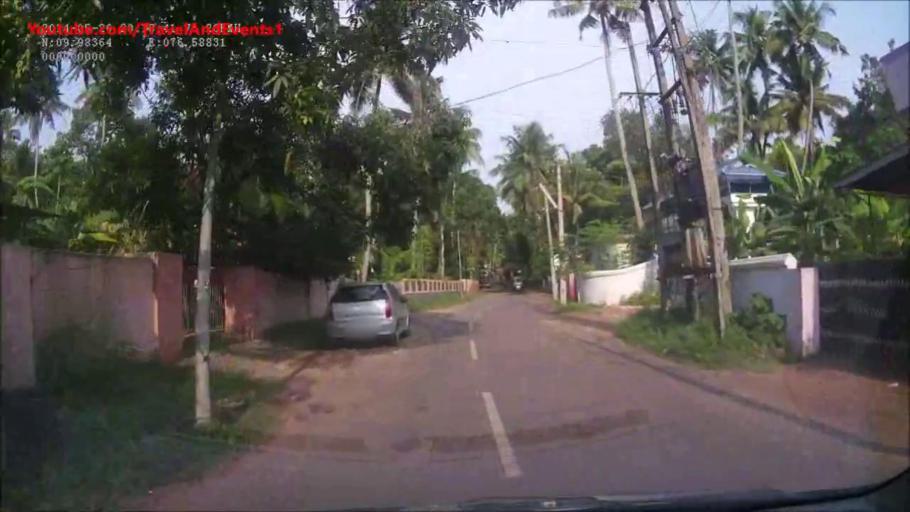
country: IN
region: Kerala
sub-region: Ernakulam
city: Muvattupula
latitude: 9.9816
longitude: 76.5912
